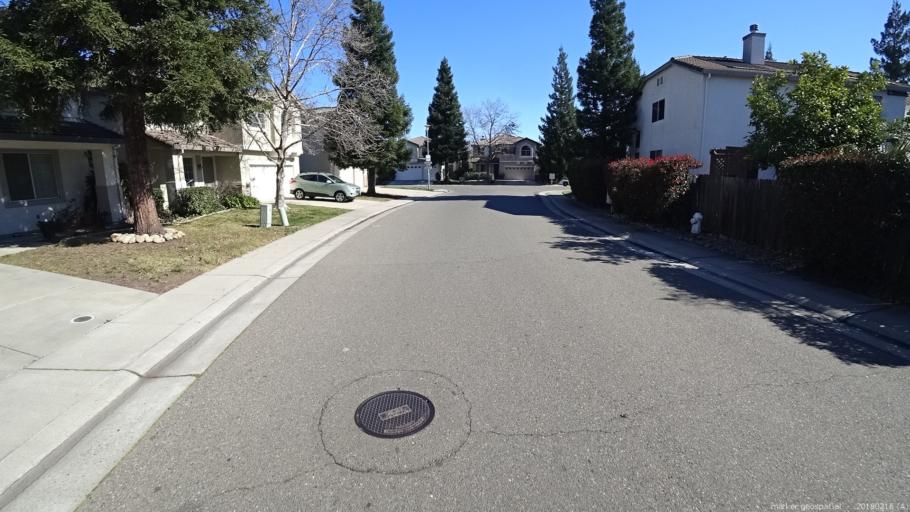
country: US
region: California
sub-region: Sacramento County
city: Gold River
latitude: 38.6189
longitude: -121.2557
